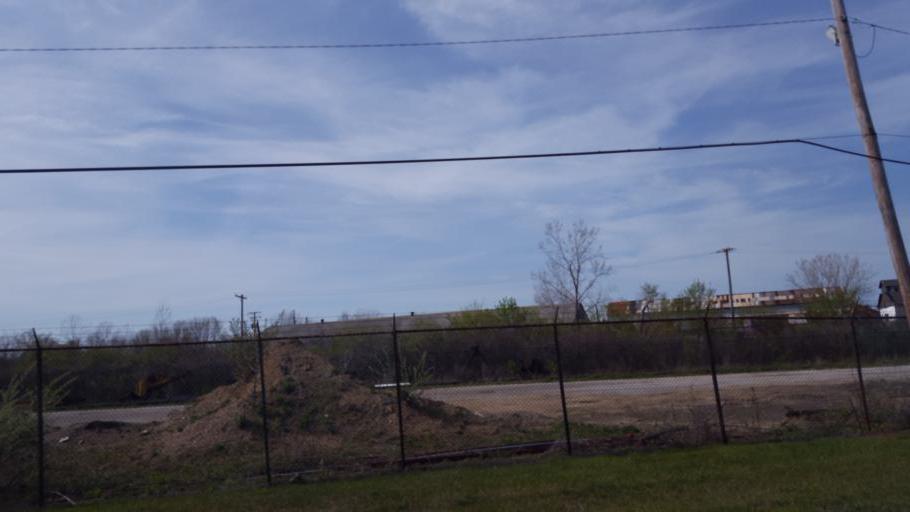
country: US
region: Ohio
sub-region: Lake County
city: Fairport Harbor
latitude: 41.7536
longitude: -81.2640
